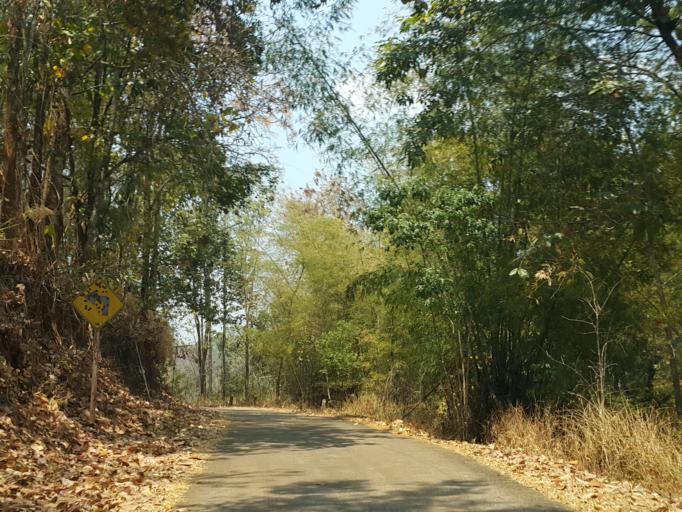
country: TH
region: Chiang Mai
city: Samoeng
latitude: 18.7992
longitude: 98.8104
